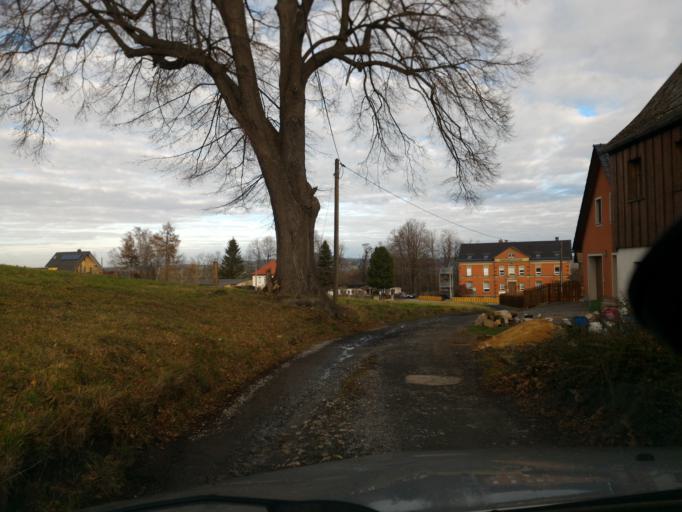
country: DE
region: Saxony
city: Grossschonau
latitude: 50.8694
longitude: 14.6480
